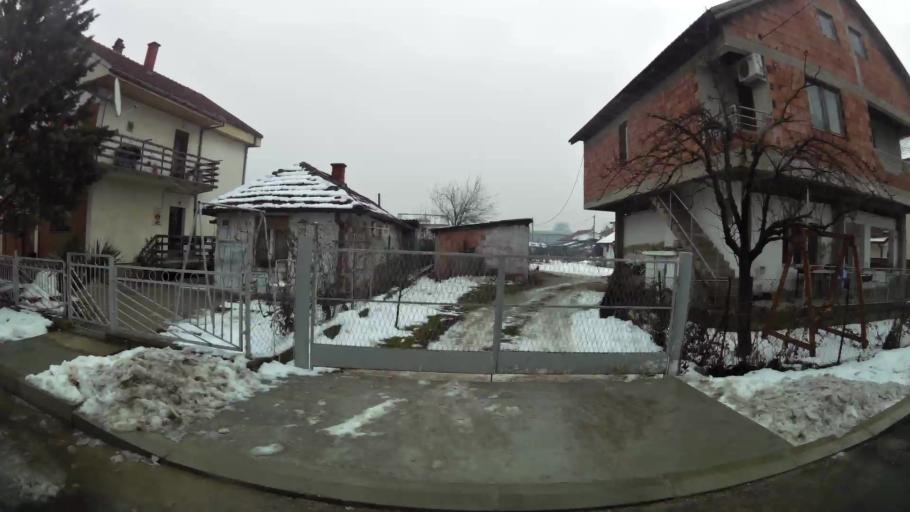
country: MK
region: Petrovec
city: Petrovec
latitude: 41.9418
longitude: 21.6105
